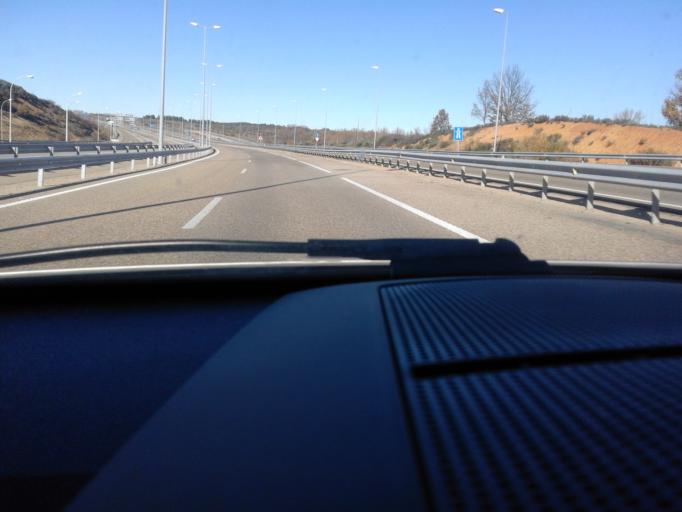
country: ES
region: Castille and Leon
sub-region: Provincia de Leon
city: Valverde de la Virgen
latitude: 42.5755
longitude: -5.6633
